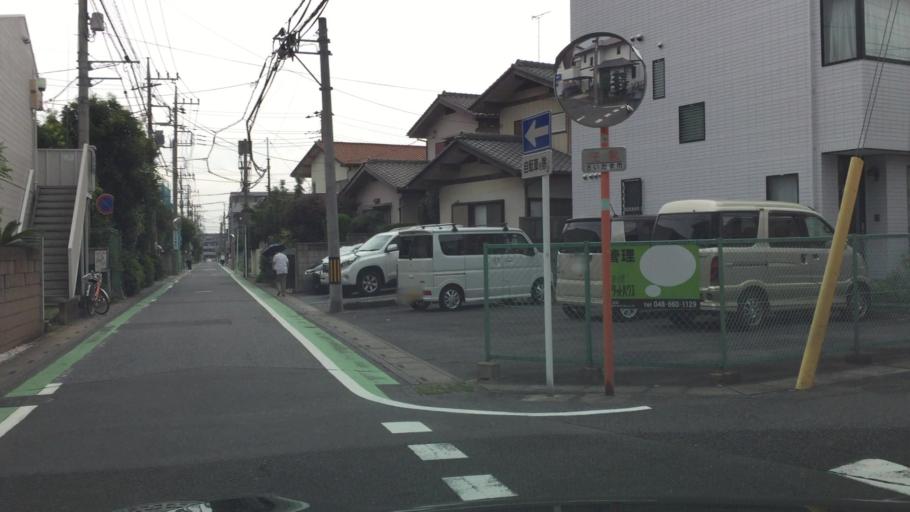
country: JP
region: Saitama
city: Yono
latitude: 35.9206
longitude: 139.6133
